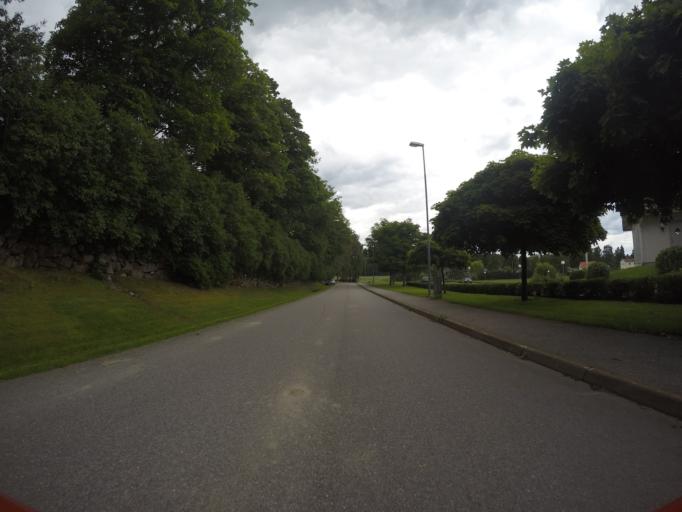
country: SE
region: Vaestra Goetaland
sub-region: Vanersborgs Kommun
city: Vargon
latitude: 58.2458
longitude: 12.4185
